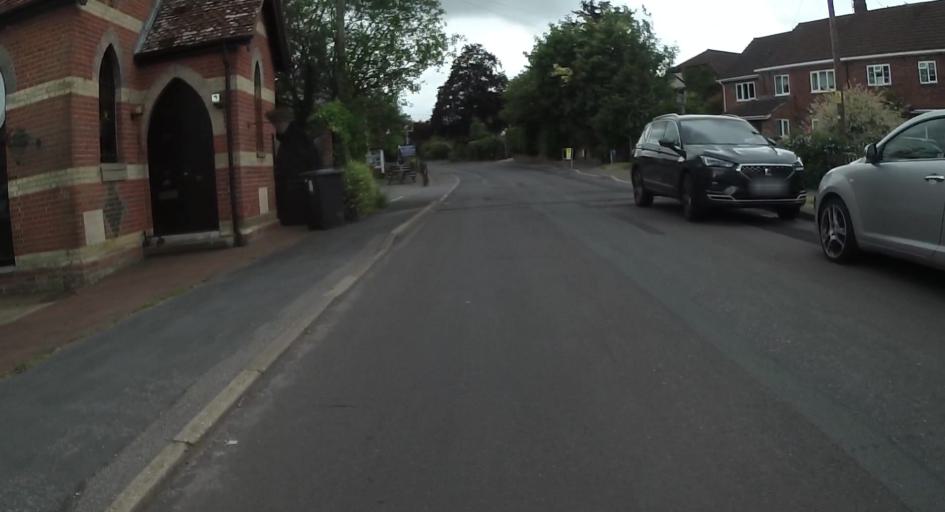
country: GB
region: England
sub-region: Hampshire
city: Fleet
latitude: 51.2366
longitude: -0.8596
